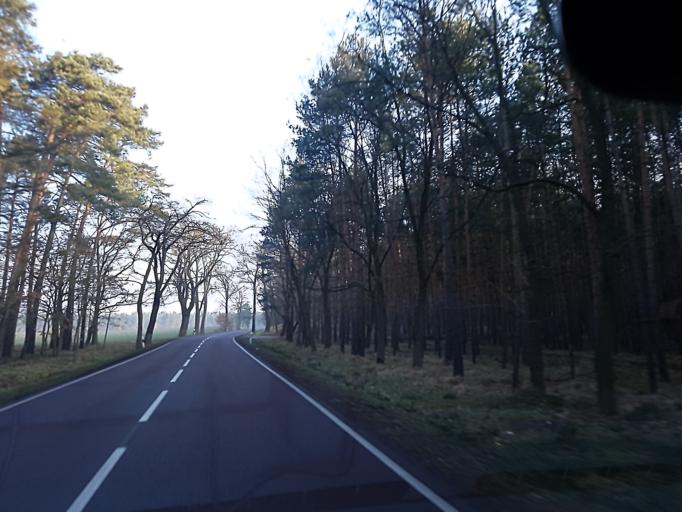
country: DE
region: Saxony-Anhalt
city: Coswig
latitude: 51.9767
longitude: 12.4667
